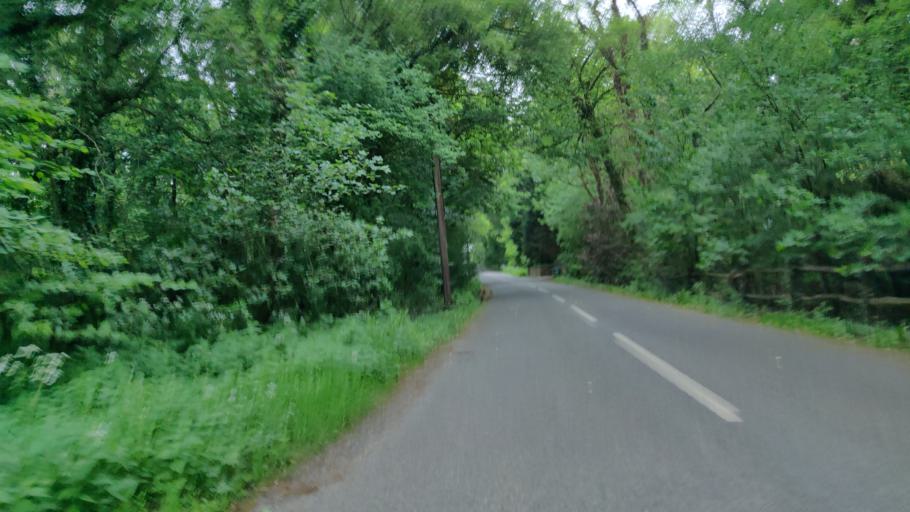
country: GB
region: England
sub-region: West Sussex
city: Partridge Green
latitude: 50.9806
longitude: -0.3007
